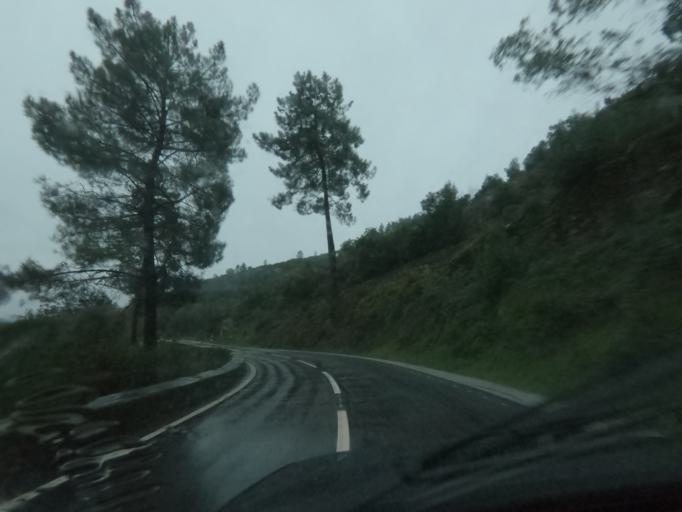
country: PT
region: Vila Real
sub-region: Sabrosa
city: Vilela
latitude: 41.2015
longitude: -7.5635
